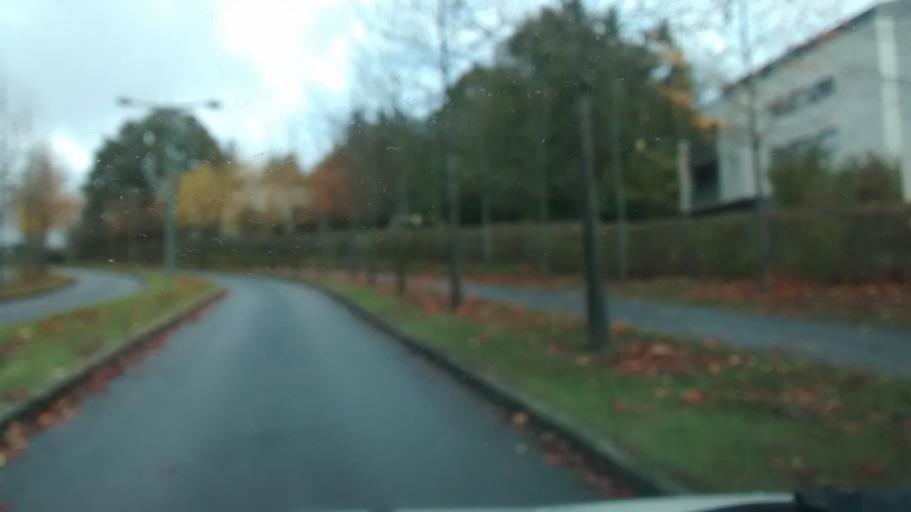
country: FR
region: Brittany
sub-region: Departement d'Ille-et-Vilaine
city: Chateaubourg
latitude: 48.1098
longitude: -1.3878
